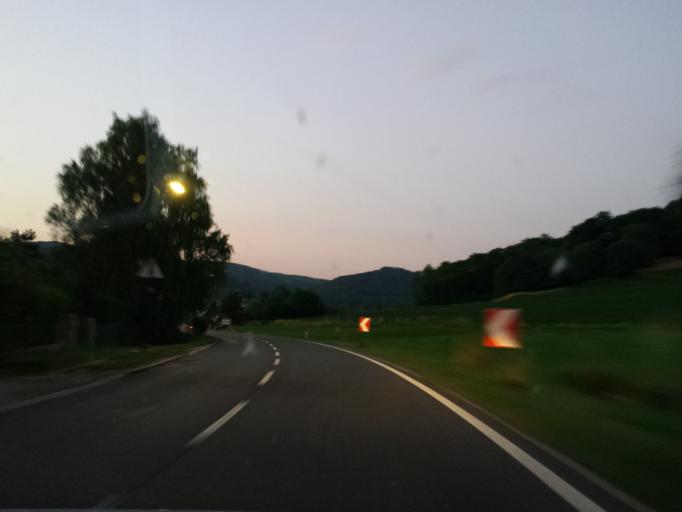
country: AT
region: Lower Austria
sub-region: Politischer Bezirk Baden
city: Alland
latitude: 48.0515
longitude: 16.0702
